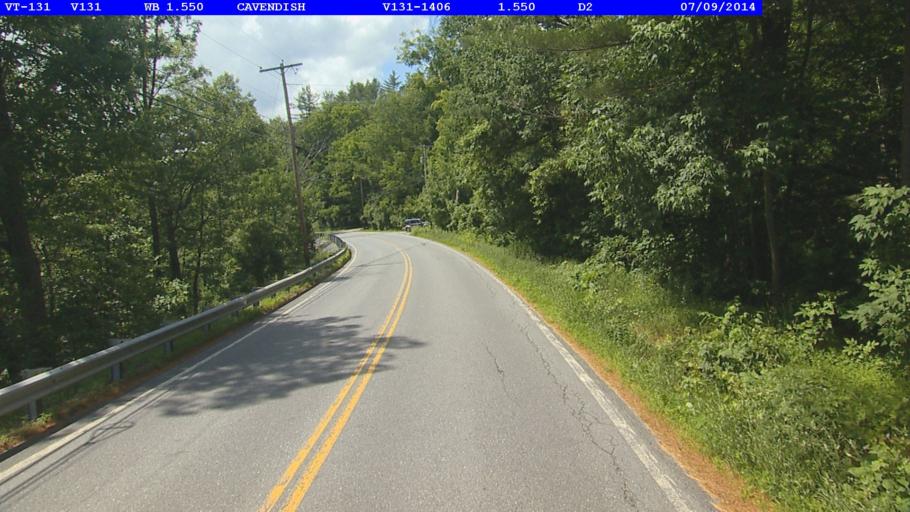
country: US
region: Vermont
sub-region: Windsor County
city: Chester
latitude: 43.3847
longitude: -72.6183
